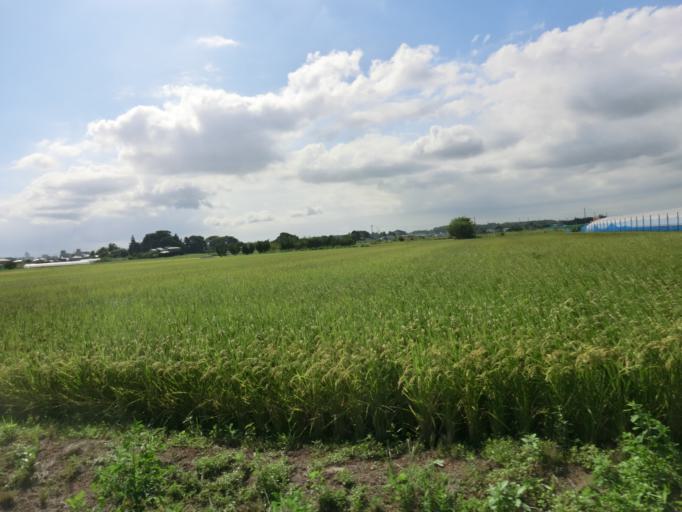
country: JP
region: Ibaraki
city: Naka
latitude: 36.0940
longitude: 140.1539
